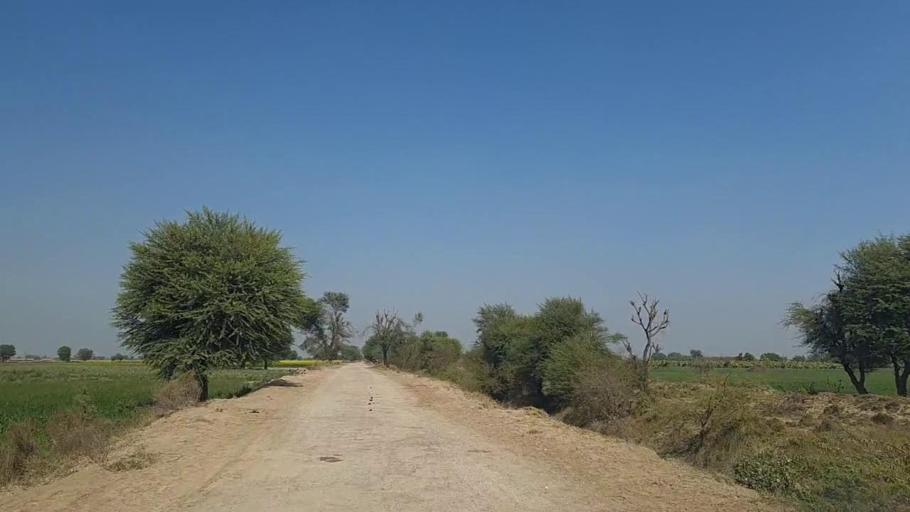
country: PK
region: Sindh
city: Shahpur Chakar
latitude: 26.1810
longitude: 68.5995
